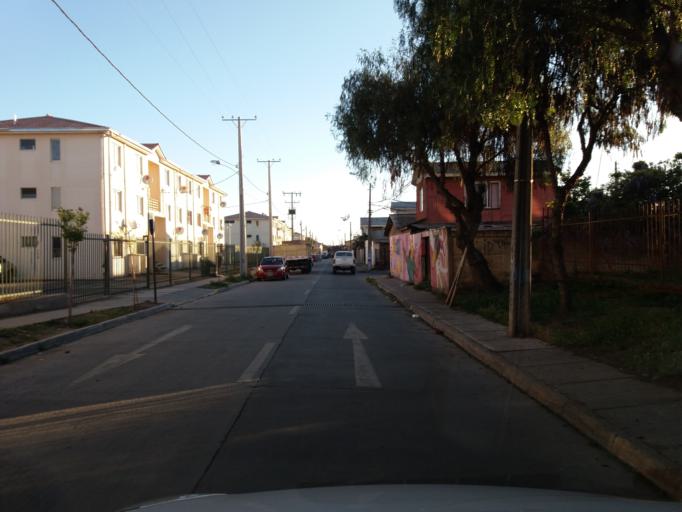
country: CL
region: Valparaiso
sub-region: Provincia de Quillota
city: Quillota
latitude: -32.8936
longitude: -71.2598
